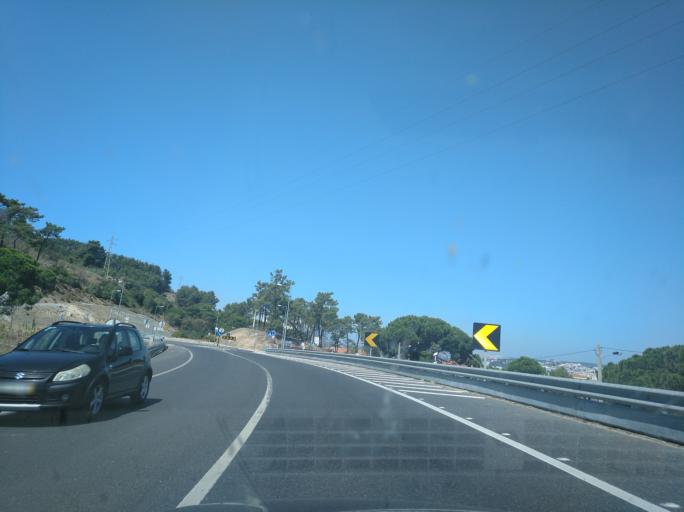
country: PT
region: Setubal
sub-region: Almada
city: Trafaria
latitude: 38.6659
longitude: -9.2305
